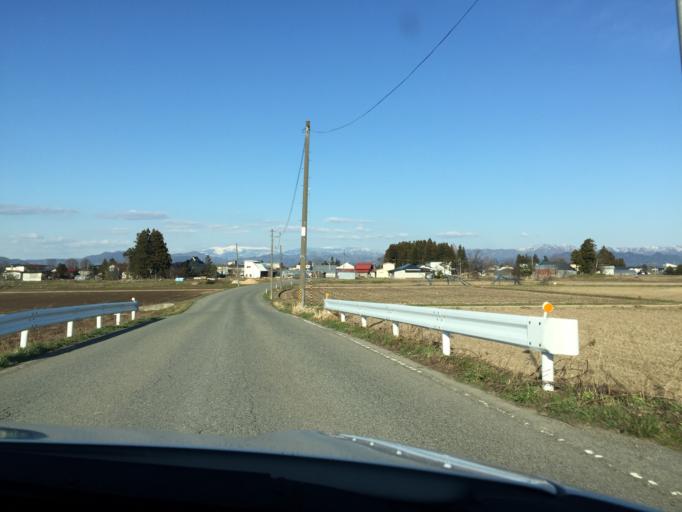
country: JP
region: Yamagata
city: Yonezawa
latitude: 37.9826
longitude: 140.0736
